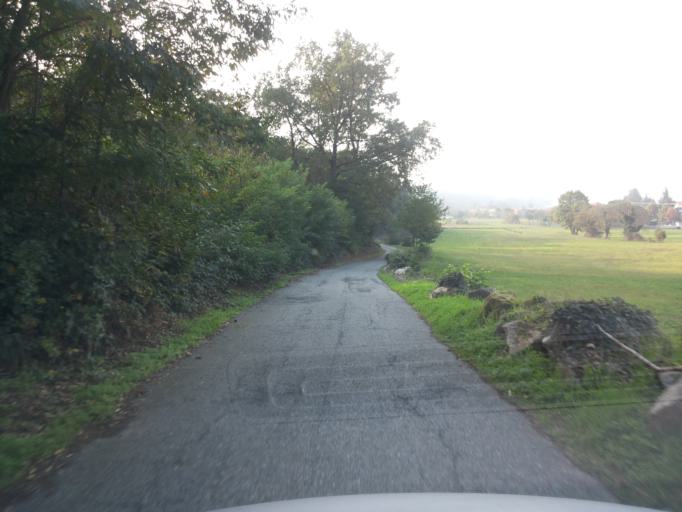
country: IT
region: Piedmont
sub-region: Provincia di Biella
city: Viverone
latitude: 45.3992
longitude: 8.0505
